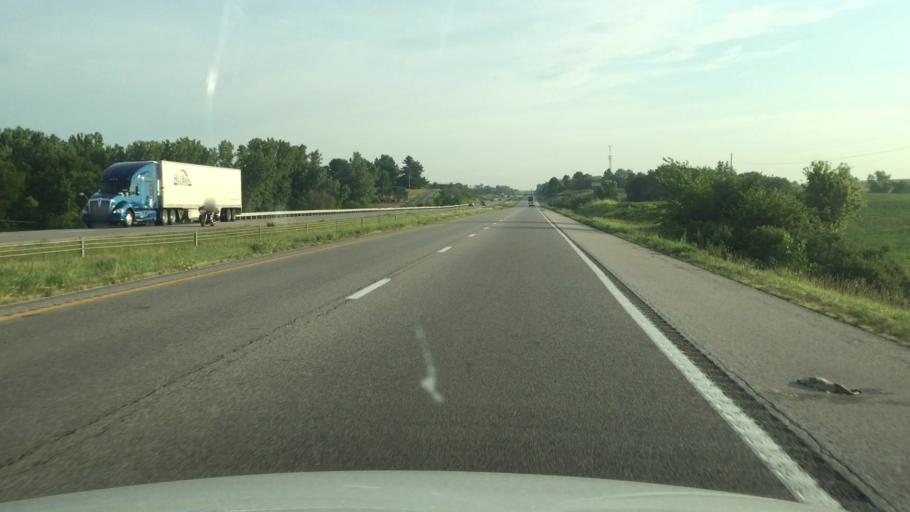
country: US
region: Kansas
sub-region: Doniphan County
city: Elwood
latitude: 39.6162
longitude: -94.7882
